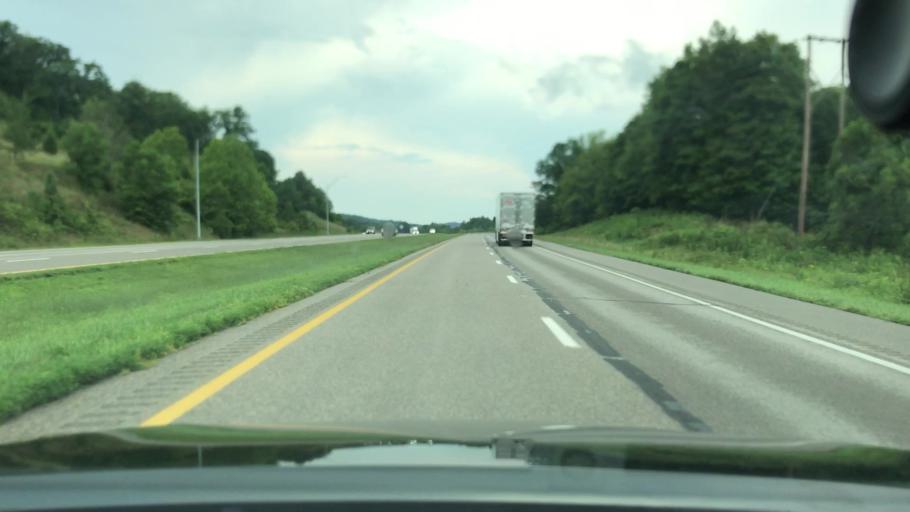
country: US
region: Ohio
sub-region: Gallia County
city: Gallipolis
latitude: 38.8475
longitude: -82.2323
